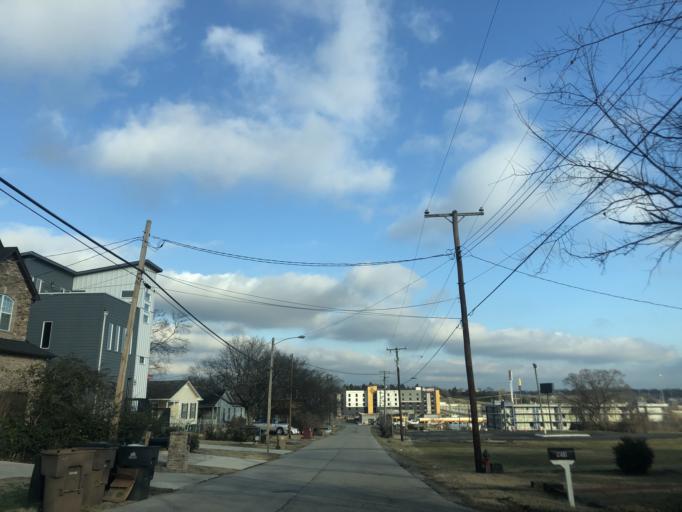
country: US
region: Tennessee
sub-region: Davidson County
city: Nashville
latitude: 36.2086
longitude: -86.7810
